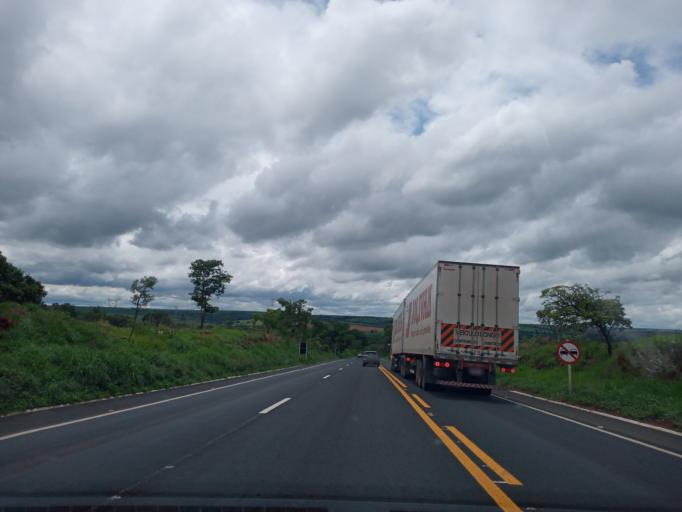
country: BR
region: Minas Gerais
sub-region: Uberaba
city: Uberaba
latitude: -19.2875
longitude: -47.6196
